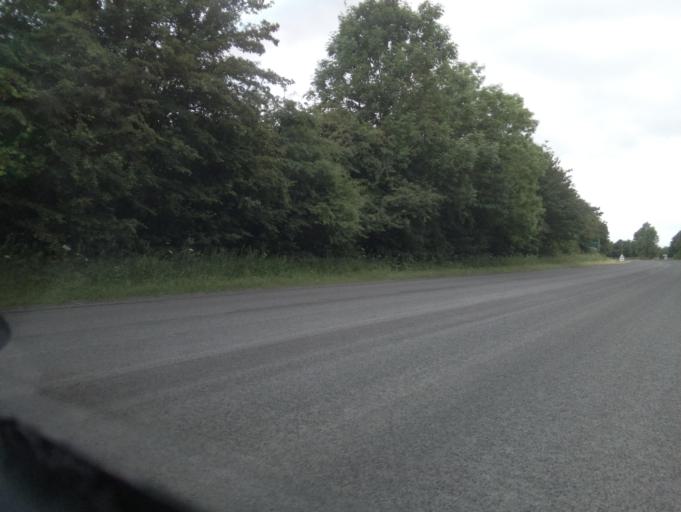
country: GB
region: England
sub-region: District of Rutland
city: Ridlington
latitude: 52.5979
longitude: -0.7954
